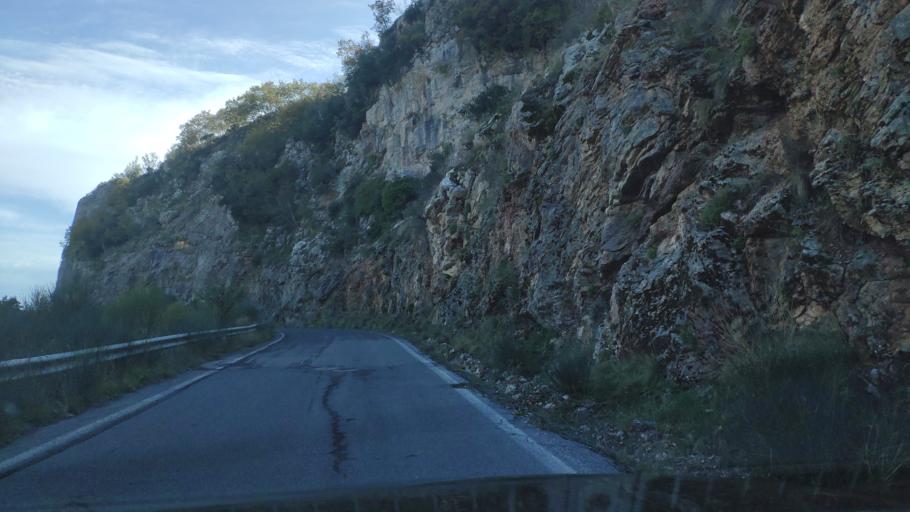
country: GR
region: Peloponnese
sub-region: Nomos Arkadias
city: Dimitsana
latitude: 37.5941
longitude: 22.0307
